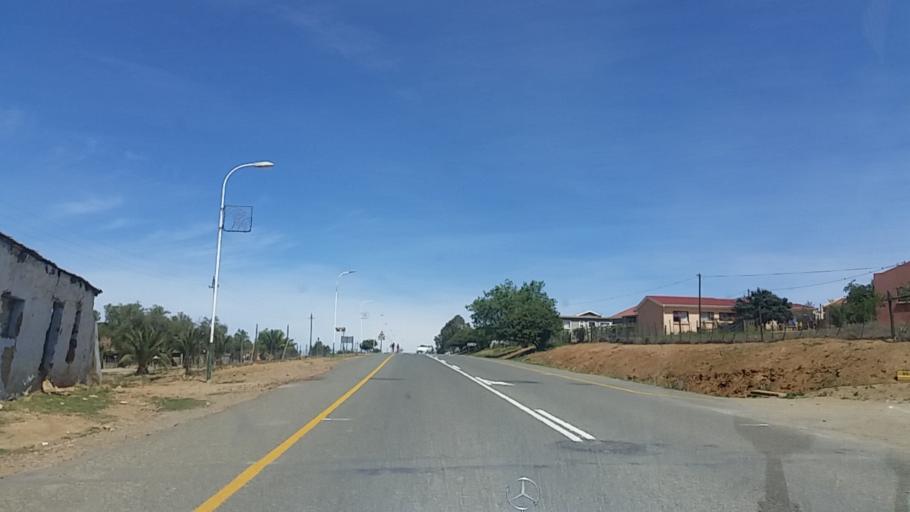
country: ZA
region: Western Cape
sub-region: Eden District Municipality
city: Knysna
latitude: -33.6597
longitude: 23.1157
